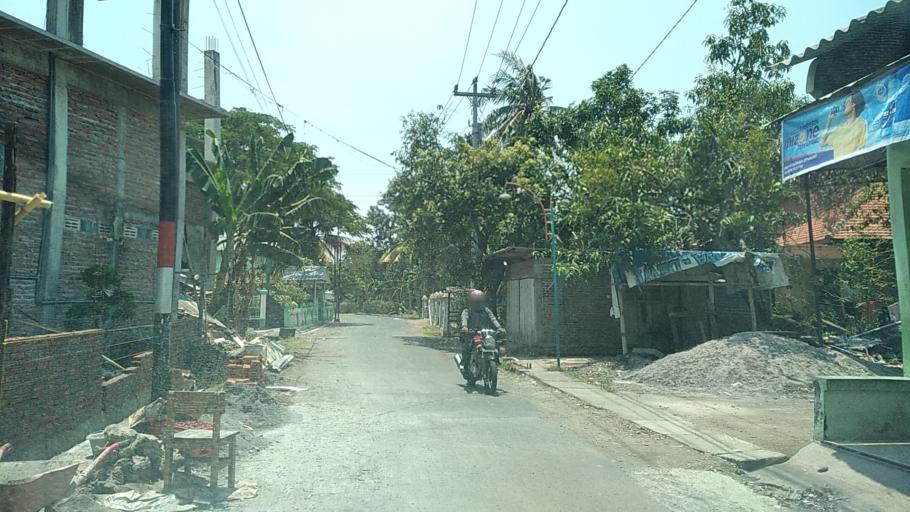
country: ID
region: Central Java
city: Semarang
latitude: -6.9817
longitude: 110.4696
